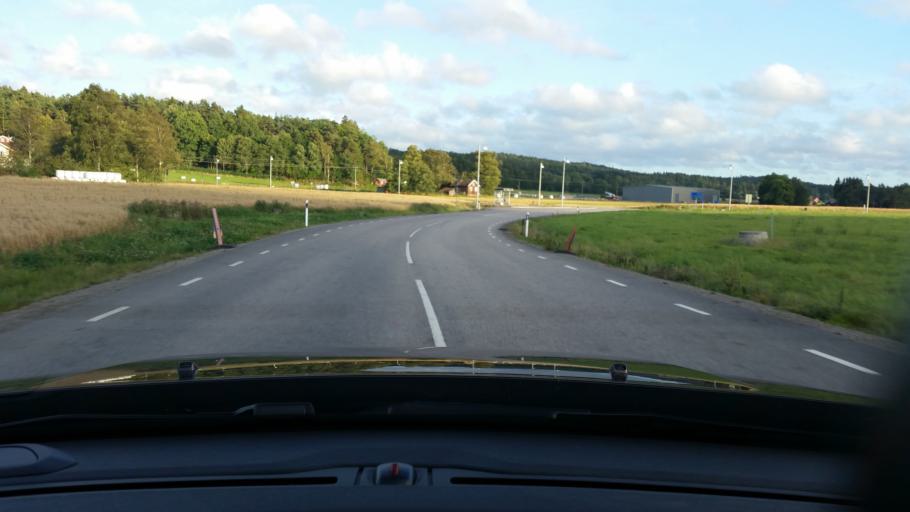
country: SE
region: Vaestra Goetaland
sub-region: Lilla Edets Kommun
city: Lilla Edet
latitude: 58.0853
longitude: 12.1582
